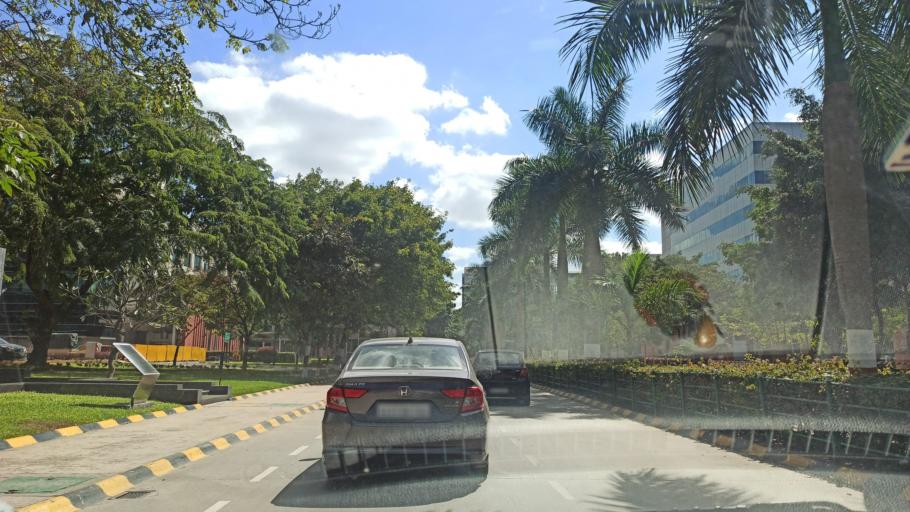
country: IN
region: Karnataka
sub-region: Bangalore Urban
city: Bangalore
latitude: 12.9269
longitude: 77.6811
